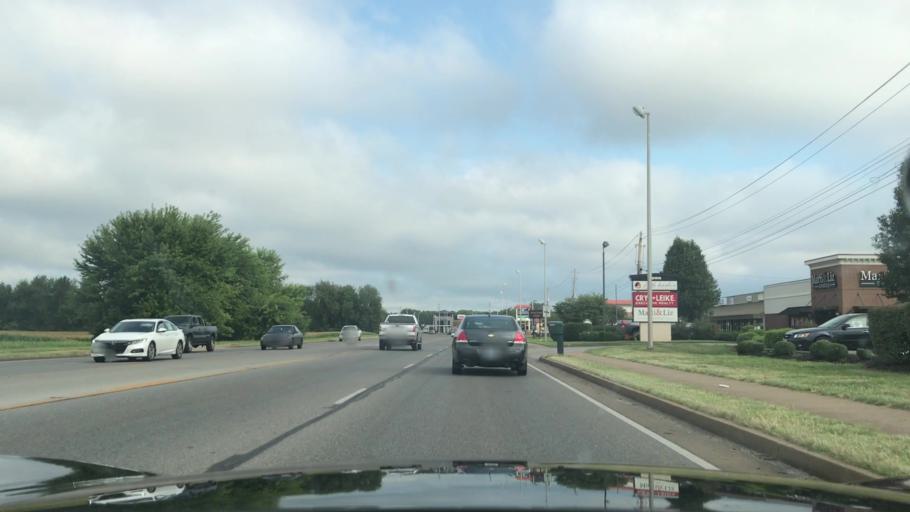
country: US
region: Kentucky
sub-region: Warren County
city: Bowling Green
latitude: 36.9578
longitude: -86.4484
